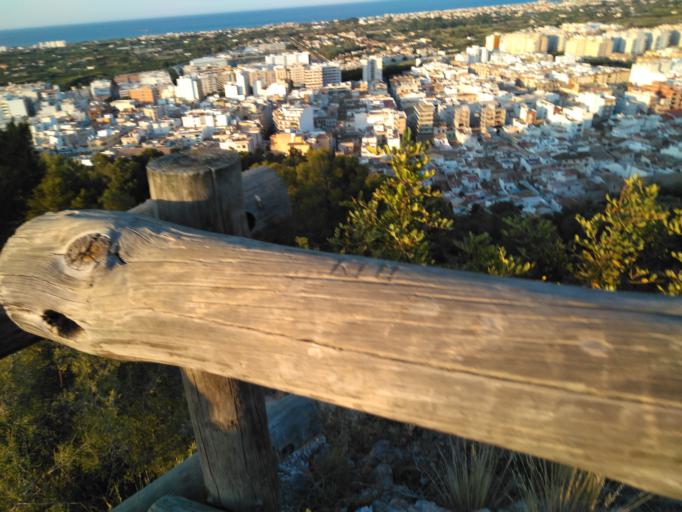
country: ES
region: Valencia
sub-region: Provincia de Valencia
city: Oliva
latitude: 38.9170
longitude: -0.1210
